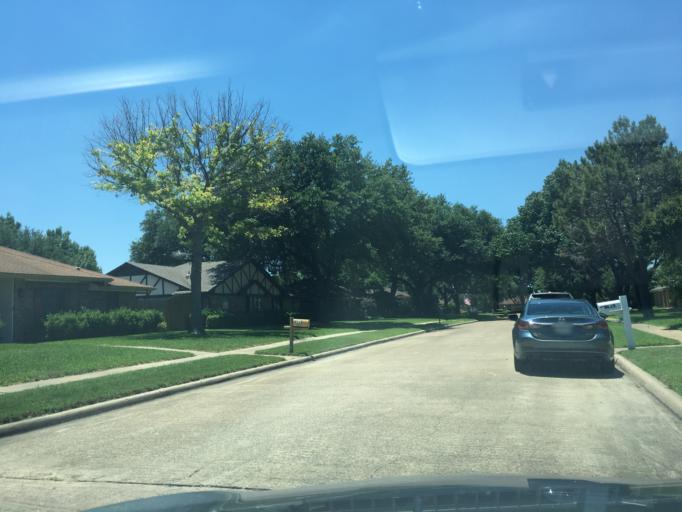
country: US
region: Texas
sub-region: Dallas County
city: Richardson
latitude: 32.9495
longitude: -96.6835
